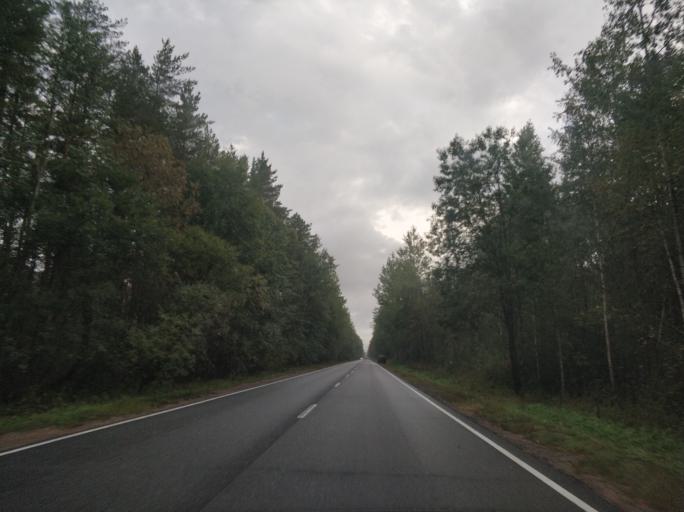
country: RU
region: Leningrad
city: Borisova Griva
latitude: 60.1456
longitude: 30.9446
